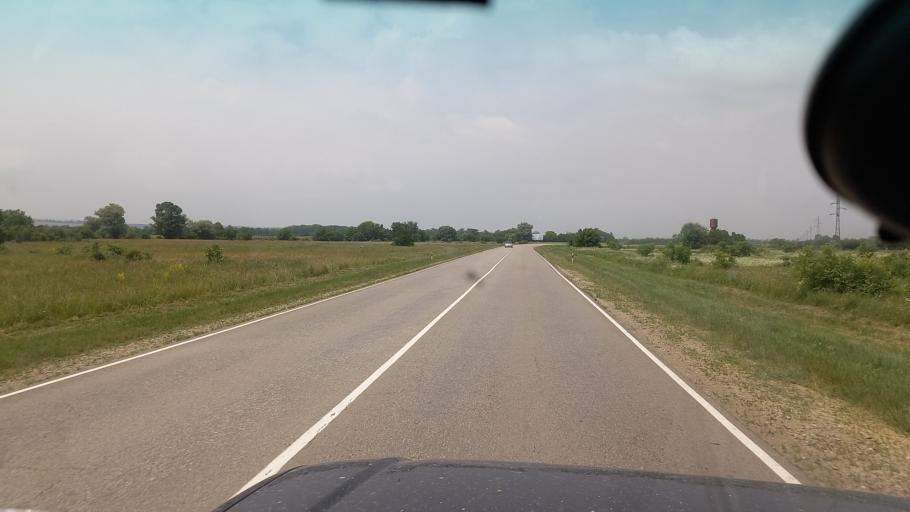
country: RU
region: Krasnodarskiy
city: Labinsk
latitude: 44.6217
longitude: 40.6961
